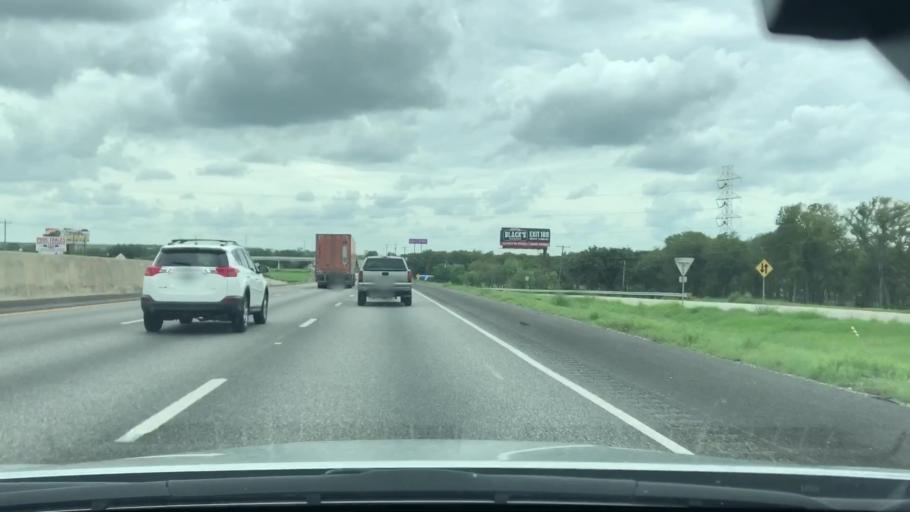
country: US
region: Texas
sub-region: Guadalupe County
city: Redwood
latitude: 29.7973
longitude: -98.0199
